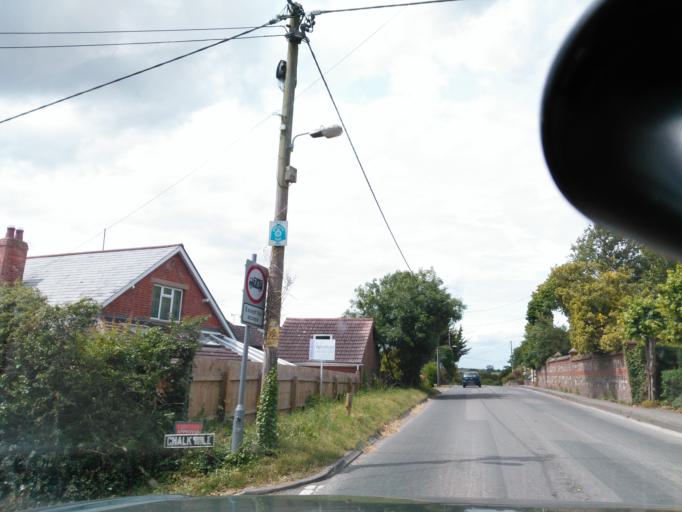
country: GB
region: England
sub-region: Wiltshire
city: Shrewton
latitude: 51.1904
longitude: -1.9002
